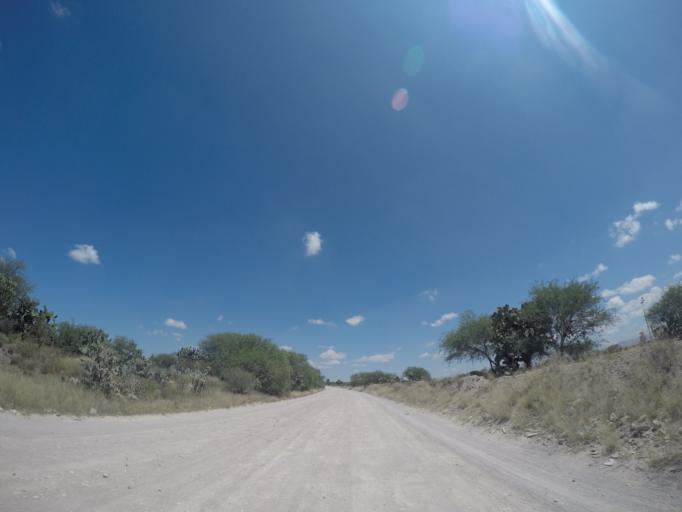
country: MX
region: San Luis Potosi
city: La Pila
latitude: 21.9910
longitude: -100.8993
